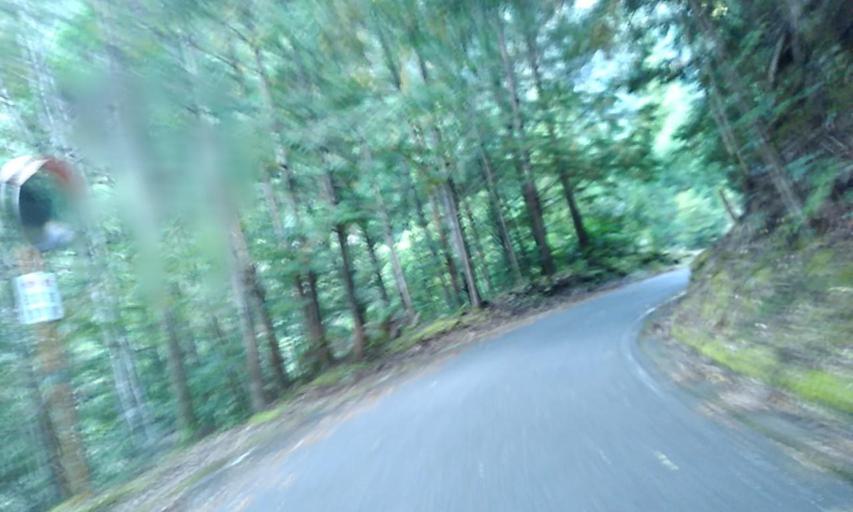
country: JP
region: Wakayama
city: Shingu
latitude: 33.9082
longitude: 135.9976
